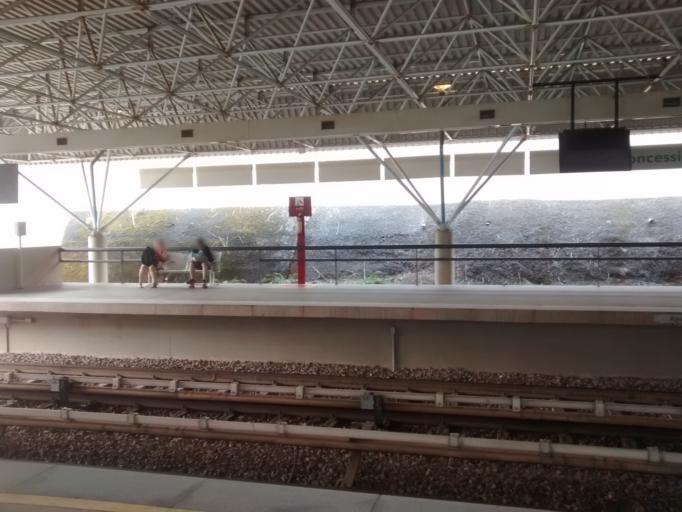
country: BR
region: Federal District
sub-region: Brasilia
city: Brasilia
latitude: -15.8350
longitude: -48.0392
